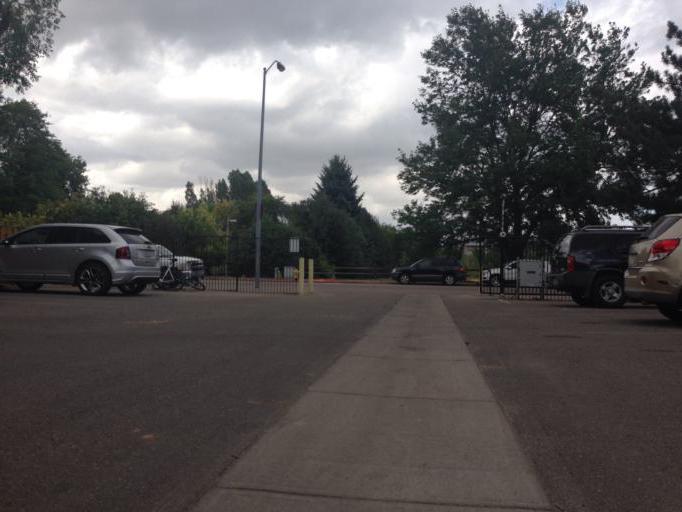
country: US
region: Colorado
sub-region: Larimer County
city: Fort Collins
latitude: 40.5685
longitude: -105.0913
